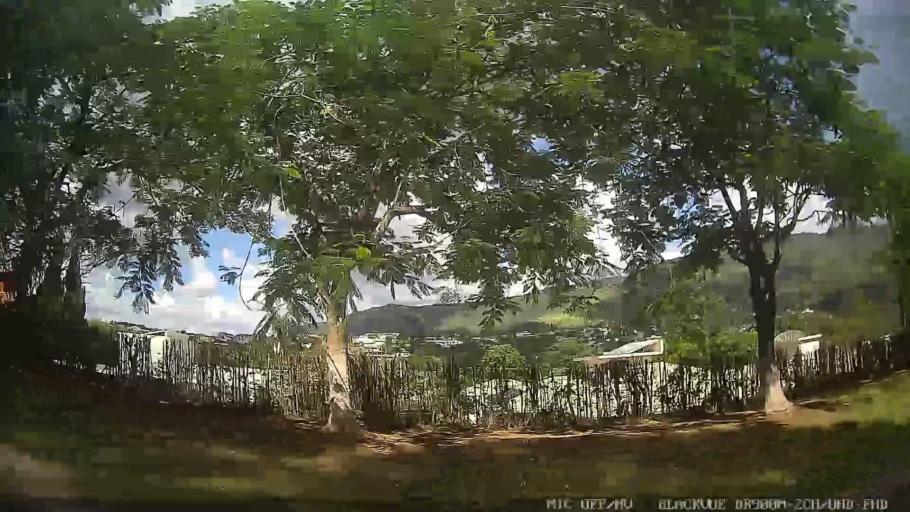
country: BR
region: Sao Paulo
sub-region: Atibaia
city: Atibaia
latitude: -23.1452
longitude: -46.5467
